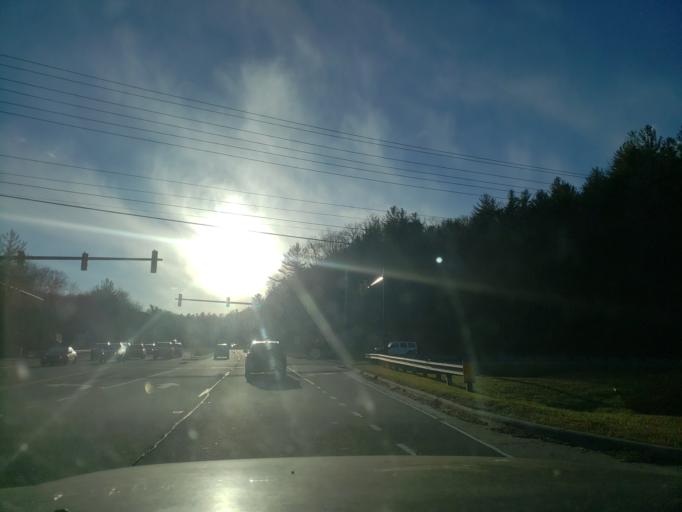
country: US
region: North Carolina
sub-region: Watauga County
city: Blowing Rock
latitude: 36.1505
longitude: -81.6597
